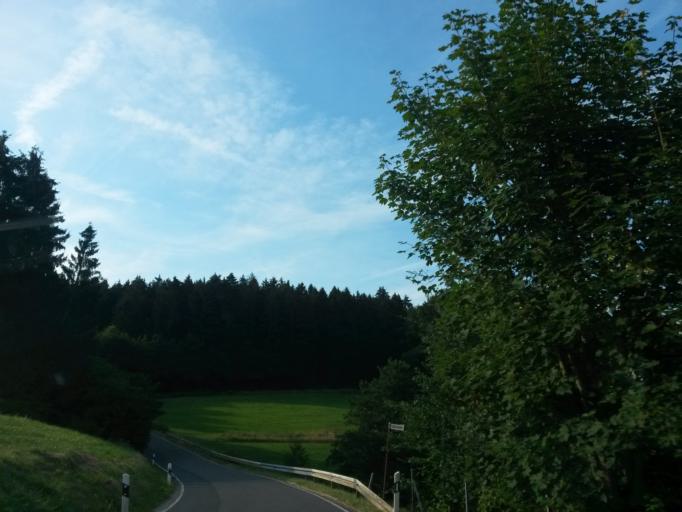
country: DE
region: North Rhine-Westphalia
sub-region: Regierungsbezirk Koln
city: Overath
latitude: 50.9695
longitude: 7.3103
